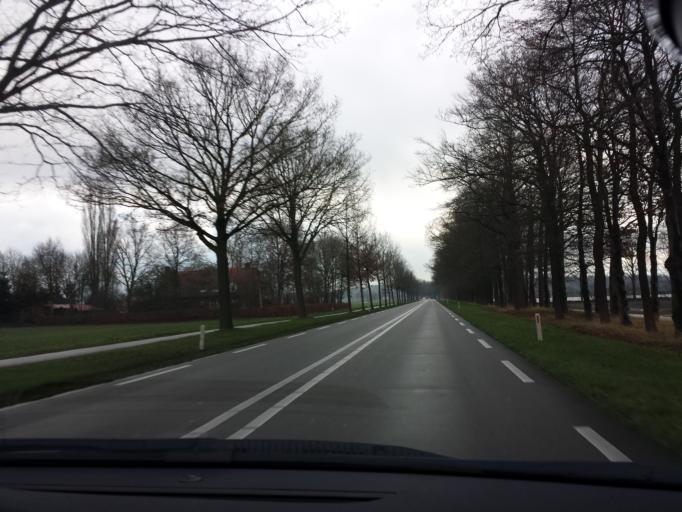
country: NL
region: North Brabant
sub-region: Gemeente Mill en Sint Hubert
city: Wilbertoord
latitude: 51.5613
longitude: 5.7791
